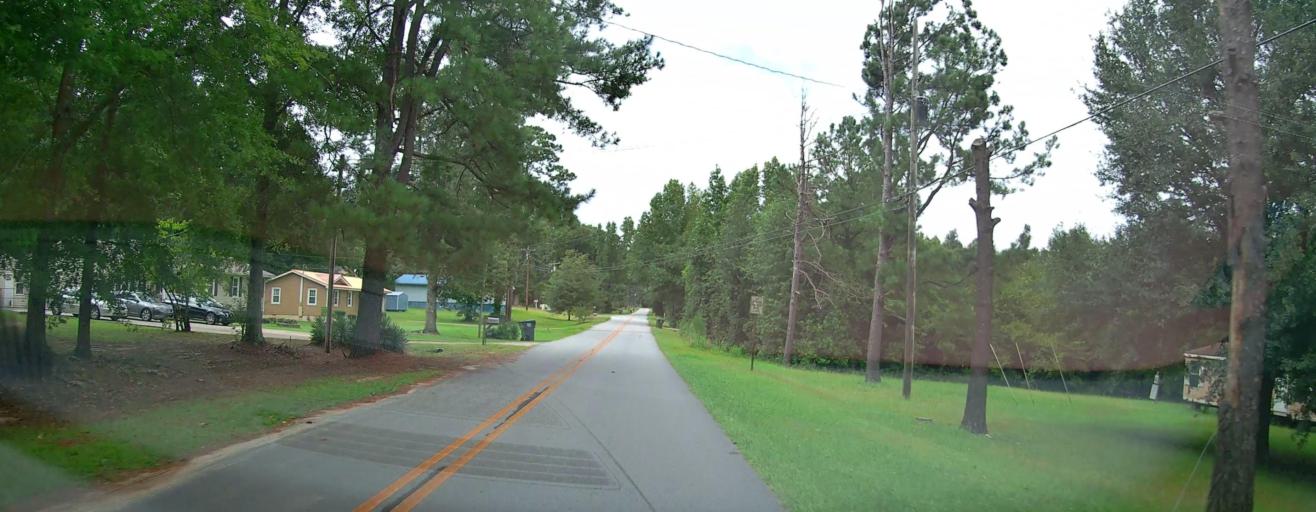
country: US
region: Georgia
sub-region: Twiggs County
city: Jeffersonville
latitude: 32.6732
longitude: -83.3216
